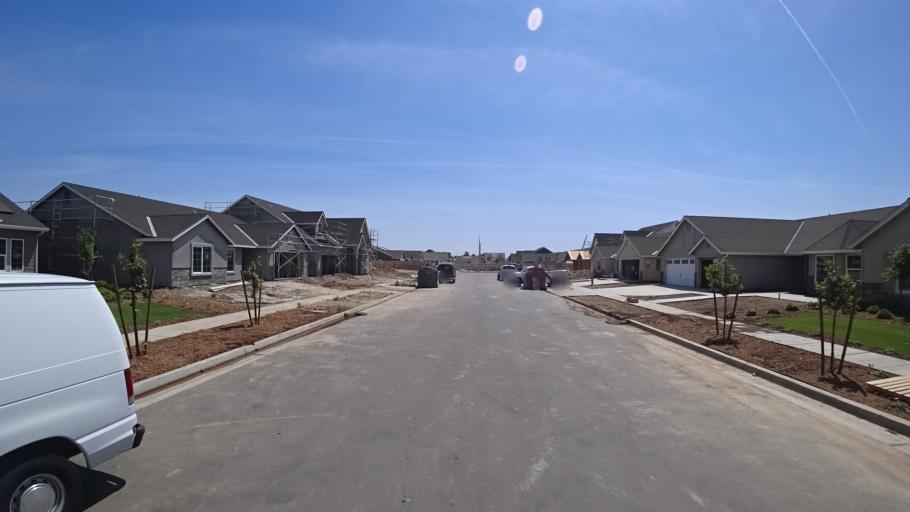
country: US
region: California
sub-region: Kings County
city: Lucerne
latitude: 36.3485
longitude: -119.6850
